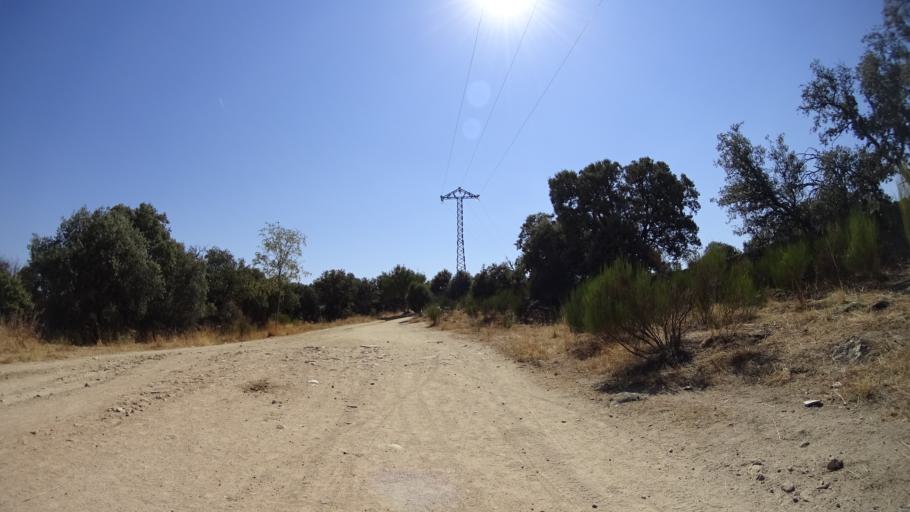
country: ES
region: Madrid
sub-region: Provincia de Madrid
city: Collado-Villalba
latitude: 40.6087
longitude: -4.0113
